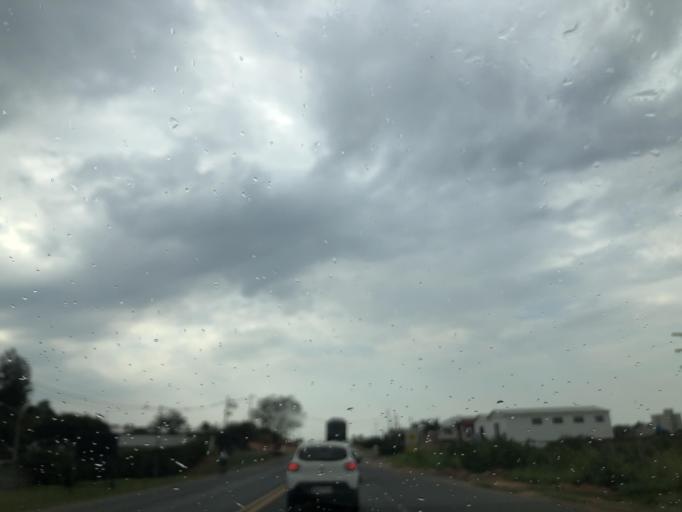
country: BR
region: Sao Paulo
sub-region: Salto De Pirapora
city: Salto de Pirapora
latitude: -23.6479
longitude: -47.5841
